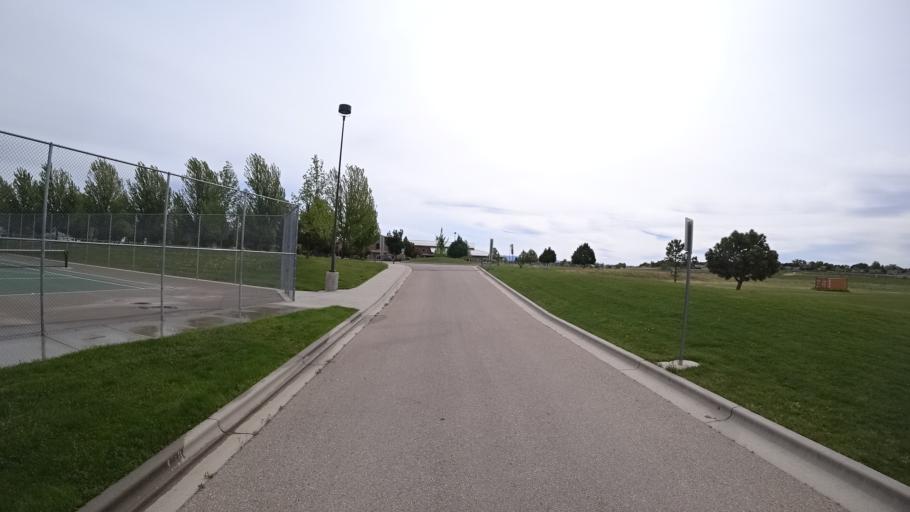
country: US
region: Idaho
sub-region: Ada County
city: Garden City
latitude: 43.5703
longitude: -116.2846
